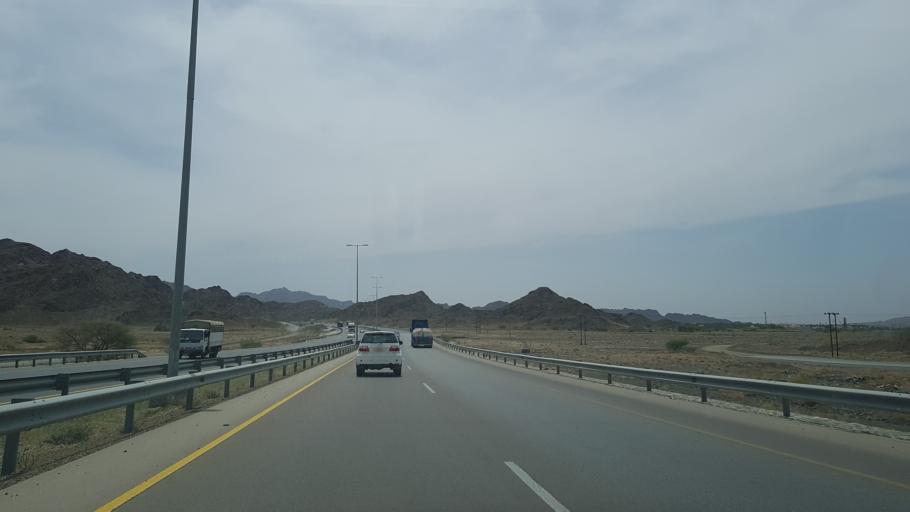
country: OM
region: Muhafazat ad Dakhiliyah
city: Izki
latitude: 22.9581
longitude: 57.7866
